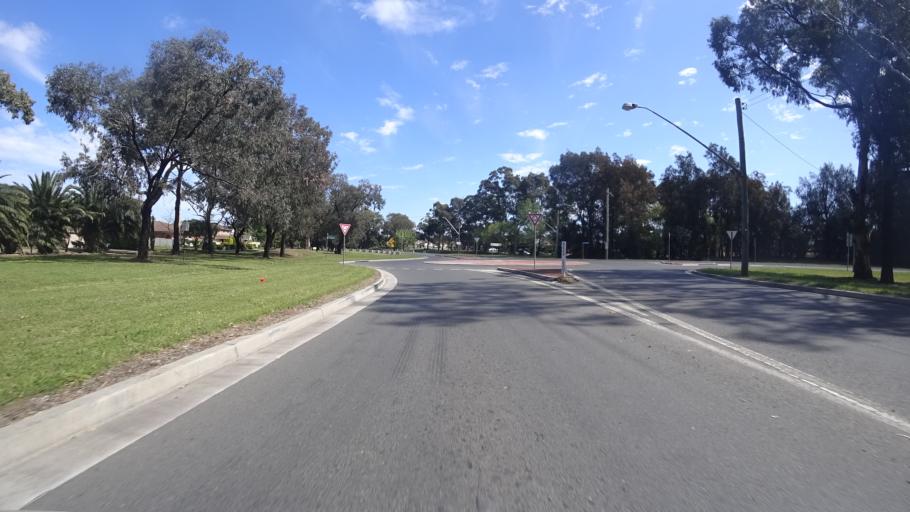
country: AU
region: New South Wales
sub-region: Fairfield
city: Chipping Norton
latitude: -33.9159
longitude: 150.9610
